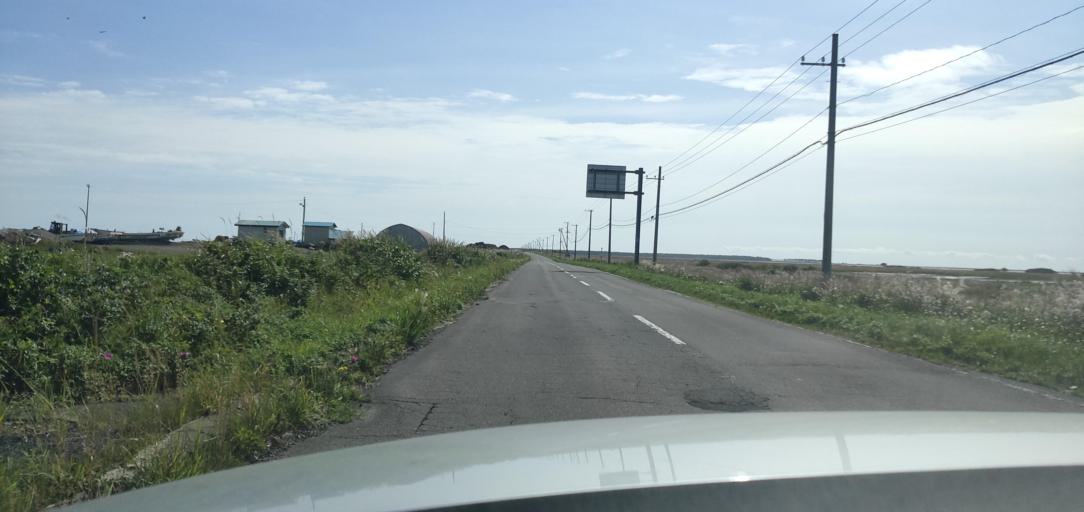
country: JP
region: Hokkaido
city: Shibetsu
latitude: 43.6209
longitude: 145.2245
